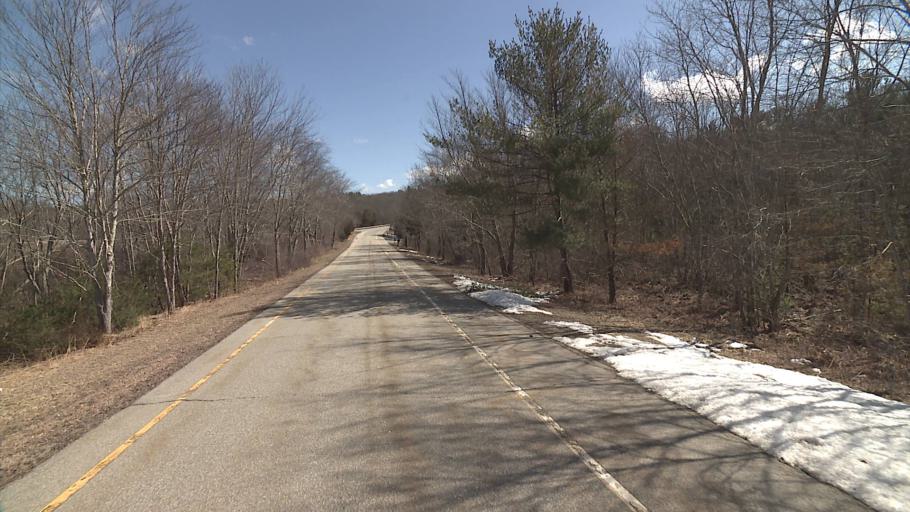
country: US
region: Connecticut
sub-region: Windham County
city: Danielson
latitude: 41.7888
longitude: -71.8450
